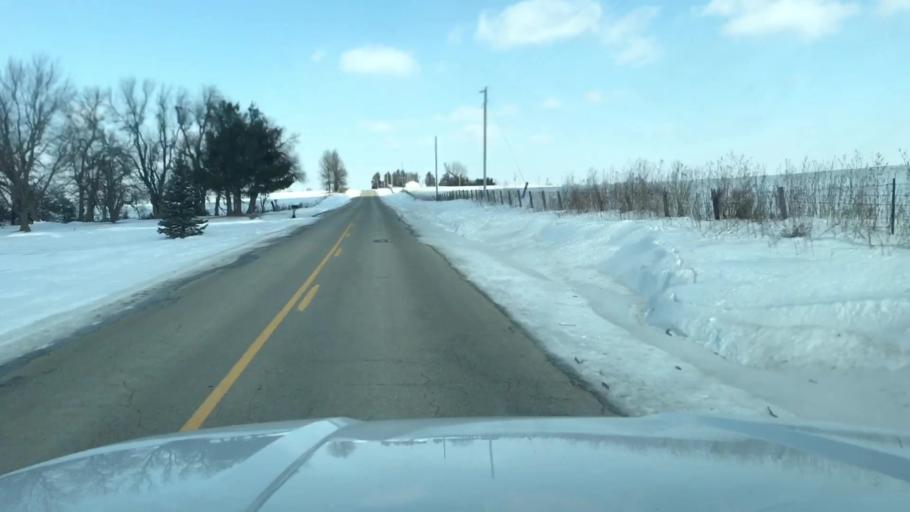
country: US
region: Missouri
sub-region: Nodaway County
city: Maryville
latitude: 40.3685
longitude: -94.7216
